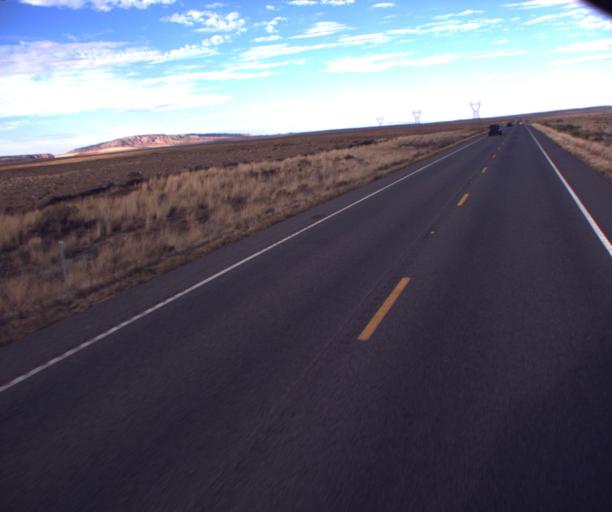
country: US
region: Arizona
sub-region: Apache County
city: Lukachukai
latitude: 36.9348
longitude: -109.2327
